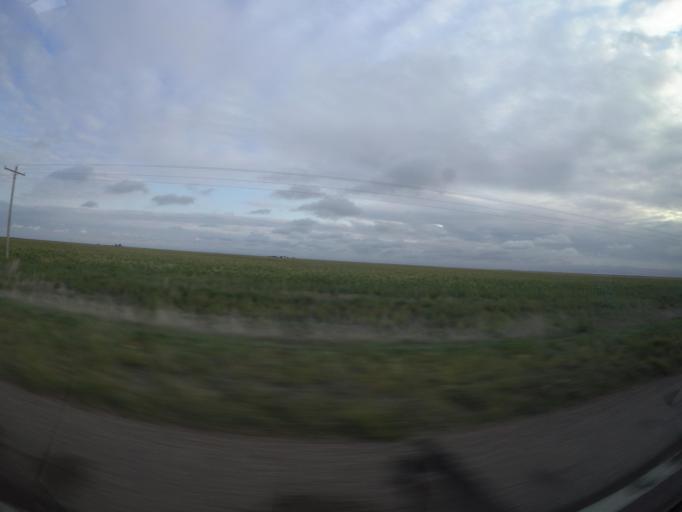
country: US
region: Colorado
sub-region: Kit Carson County
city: Burlington
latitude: 39.6573
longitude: -102.4464
